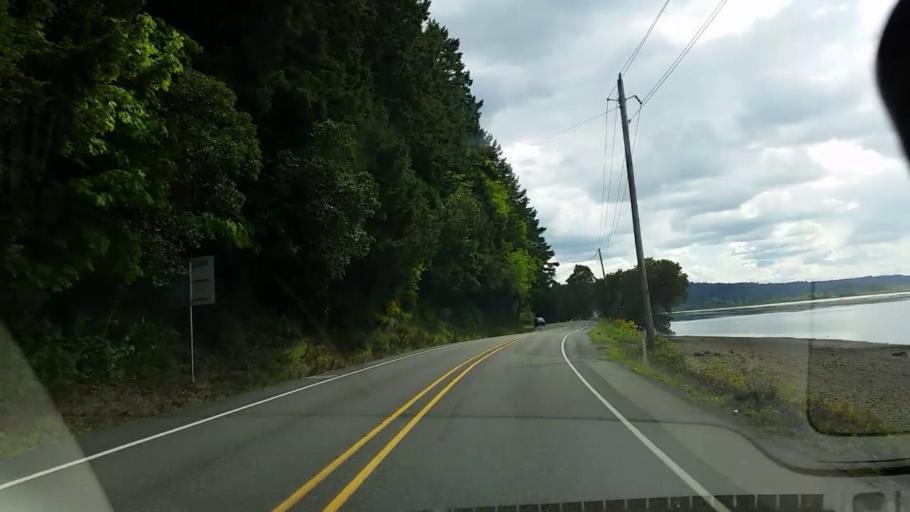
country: US
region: Washington
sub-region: Mason County
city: Shelton
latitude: 47.3552
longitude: -123.1060
